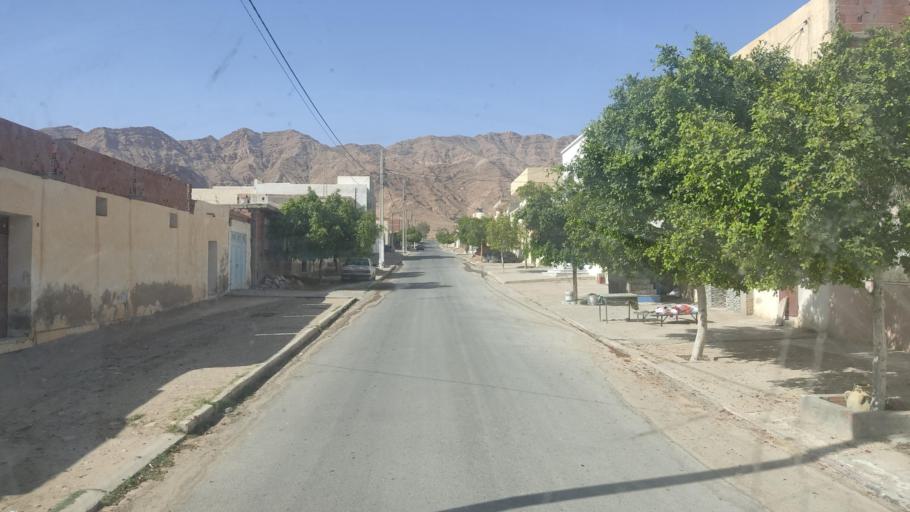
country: TN
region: Gafsa
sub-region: Gafsa Municipality
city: Gafsa
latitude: 34.3377
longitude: 8.9232
